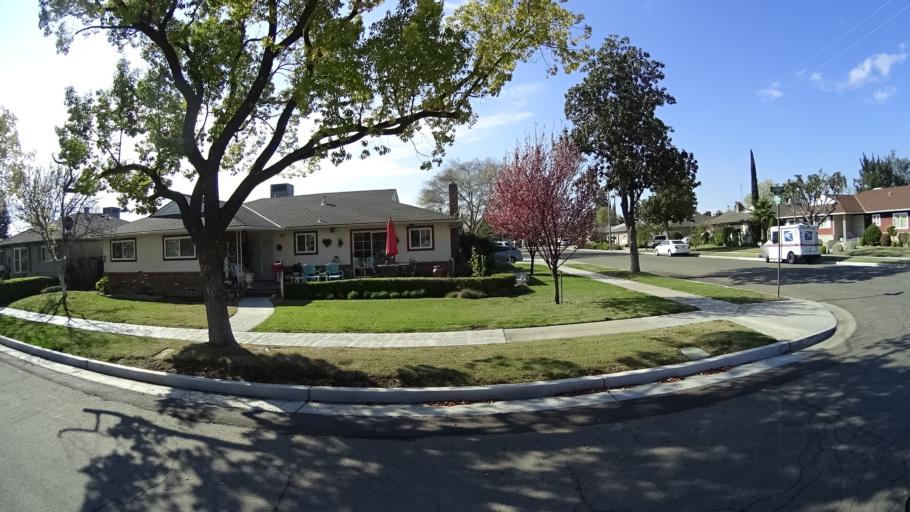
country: US
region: California
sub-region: Fresno County
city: Clovis
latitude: 36.8260
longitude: -119.7570
